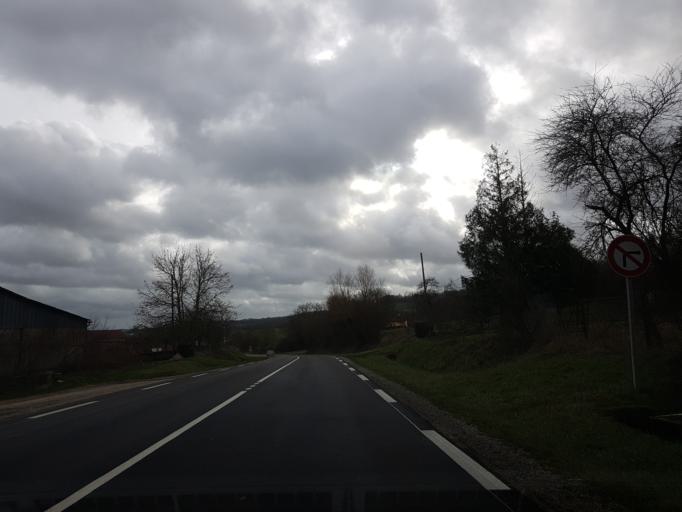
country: FR
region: Champagne-Ardenne
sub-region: Departement de la Haute-Marne
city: Langres
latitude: 47.8643
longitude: 5.3425
